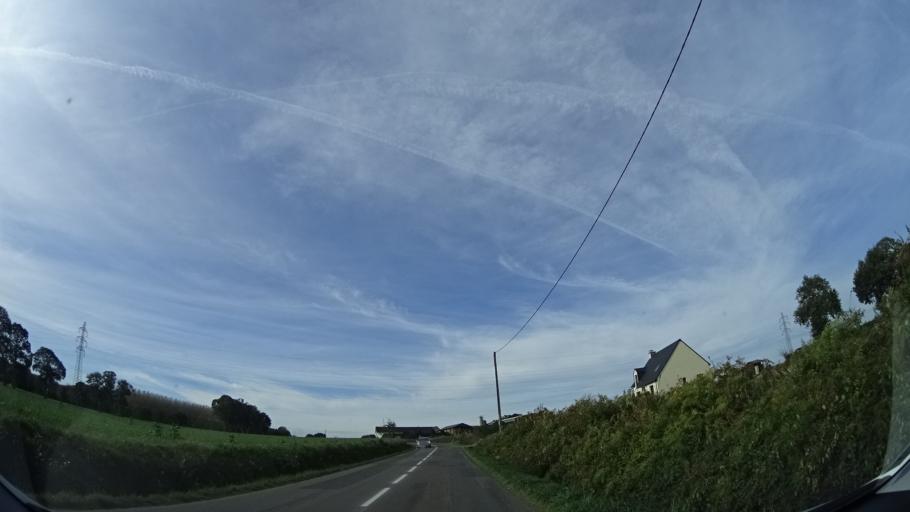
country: FR
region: Brittany
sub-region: Departement d'Ille-et-Vilaine
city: La Meziere
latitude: 48.2169
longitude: -1.7282
